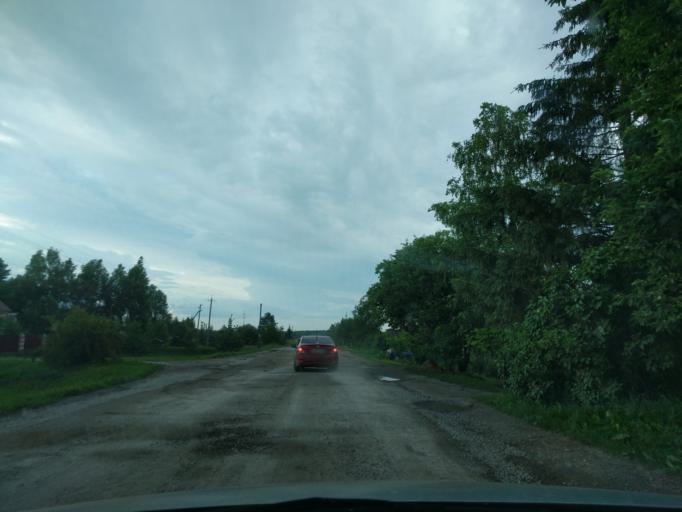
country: RU
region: Kaluga
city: Myatlevo
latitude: 54.7918
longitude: 35.7367
